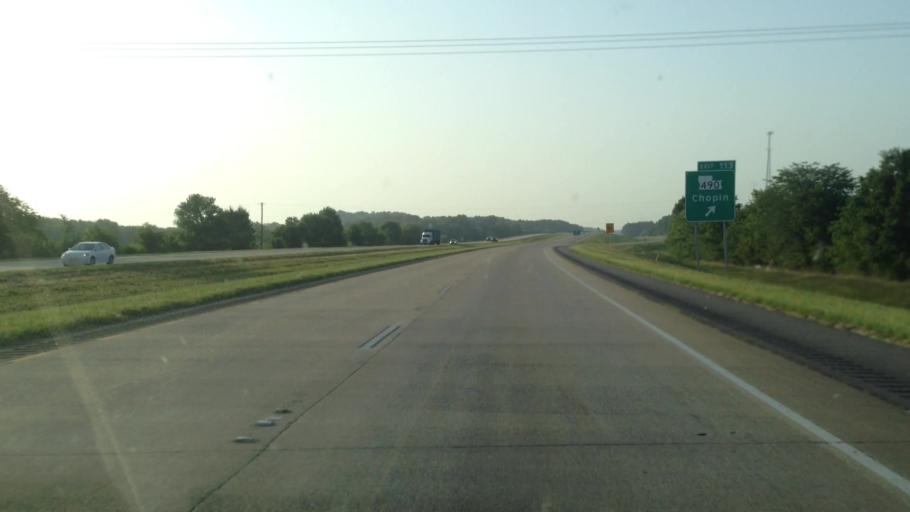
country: US
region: Louisiana
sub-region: Grant Parish
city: Colfax
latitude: 31.4992
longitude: -92.8684
